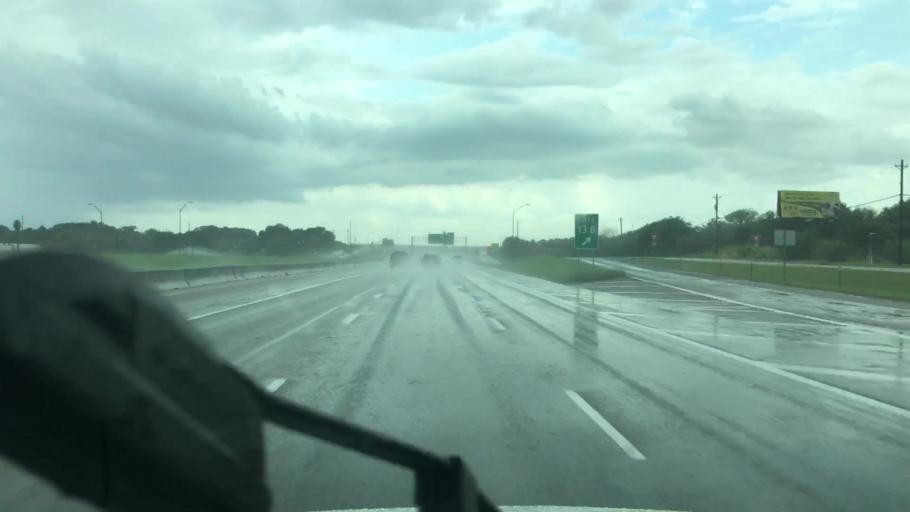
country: US
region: Texas
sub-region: Nueces County
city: Robstown
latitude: 27.8582
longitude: -97.6054
